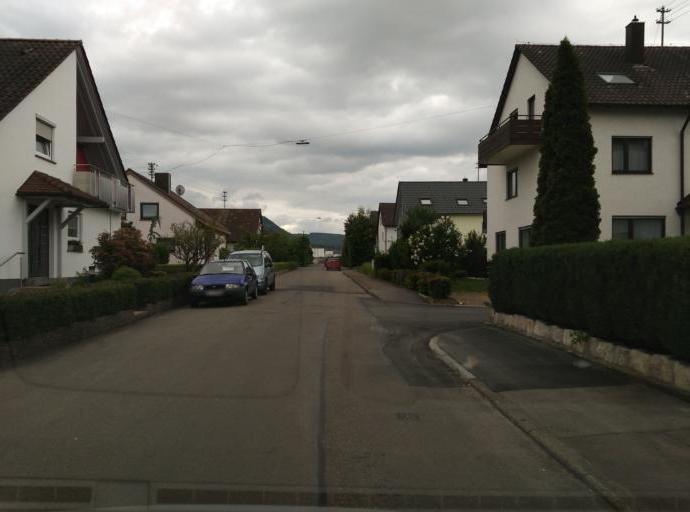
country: DE
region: Baden-Wuerttemberg
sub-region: Regierungsbezirk Stuttgart
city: Frickenhausen
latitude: 48.5897
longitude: 9.3650
